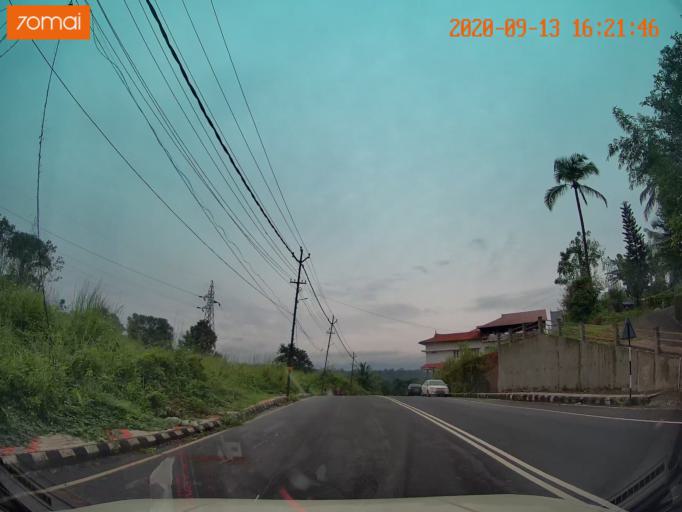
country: IN
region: Kerala
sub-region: Kottayam
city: Lalam
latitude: 9.7103
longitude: 76.6677
